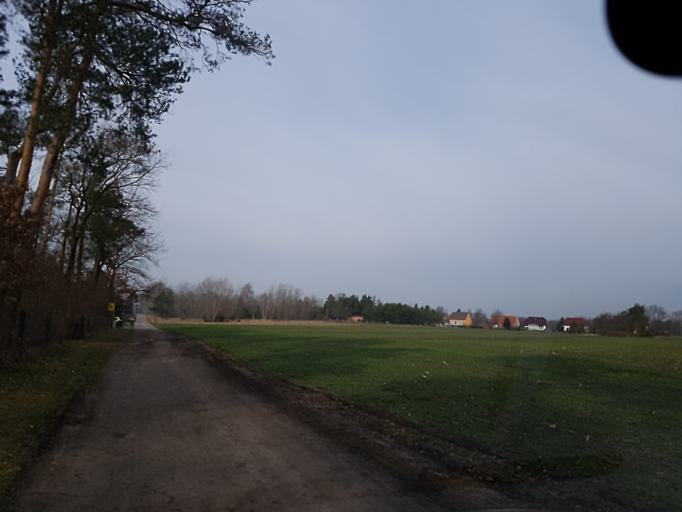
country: DE
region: Brandenburg
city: Ruckersdorf
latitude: 51.5905
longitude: 13.5522
